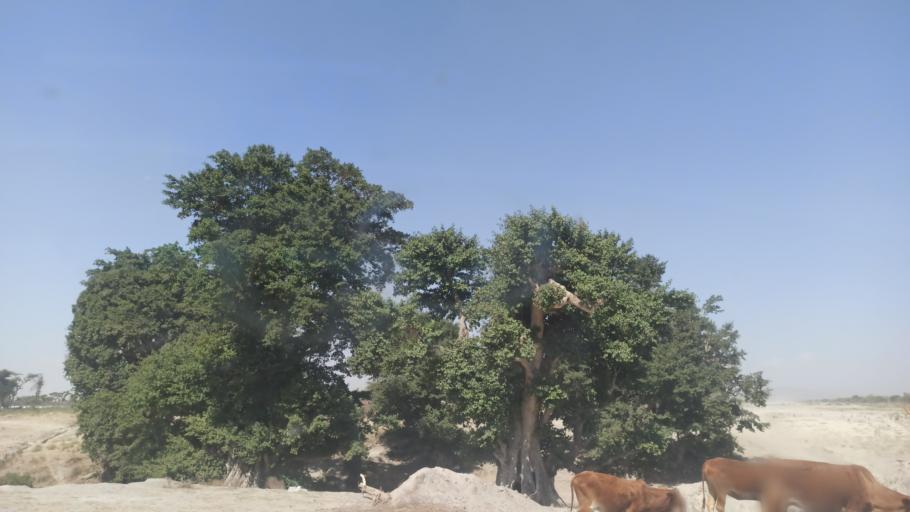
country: ET
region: Oromiya
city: Ziway
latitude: 7.7040
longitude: 38.6395
